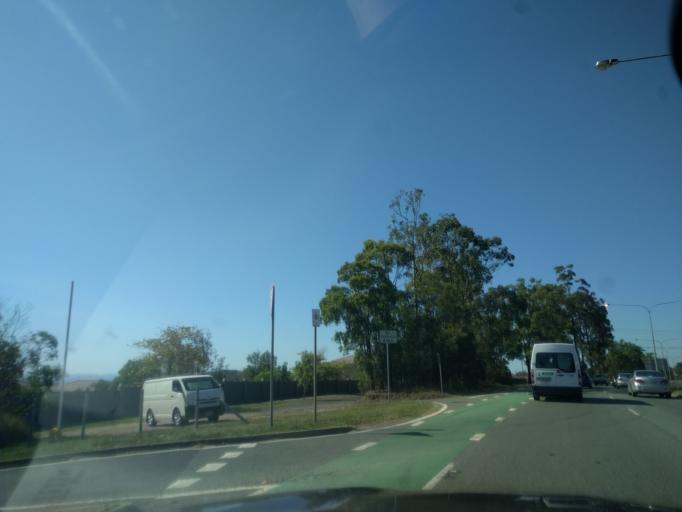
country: AU
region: Queensland
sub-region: Brisbane
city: Sunnybank Hills
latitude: -27.6383
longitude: 153.0447
